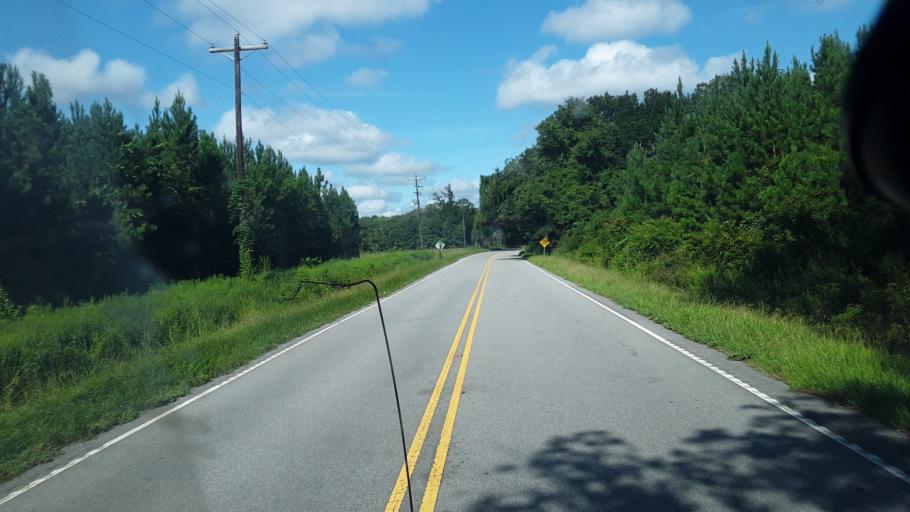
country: US
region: South Carolina
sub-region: Jasper County
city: Ridgeland
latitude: 32.5916
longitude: -80.9766
